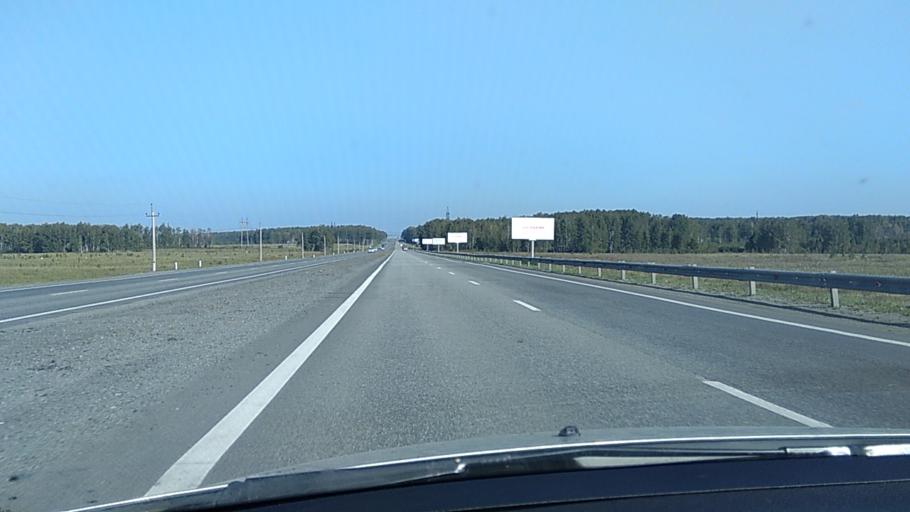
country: RU
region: Chelyabinsk
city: Poletayevo
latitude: 55.0053
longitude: 61.1716
